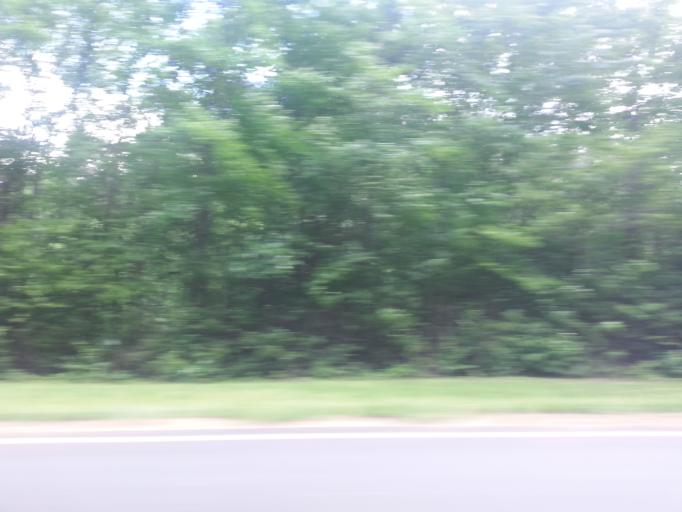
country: US
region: Georgia
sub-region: Towns County
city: Hiawassee
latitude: 34.8381
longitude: -83.7714
